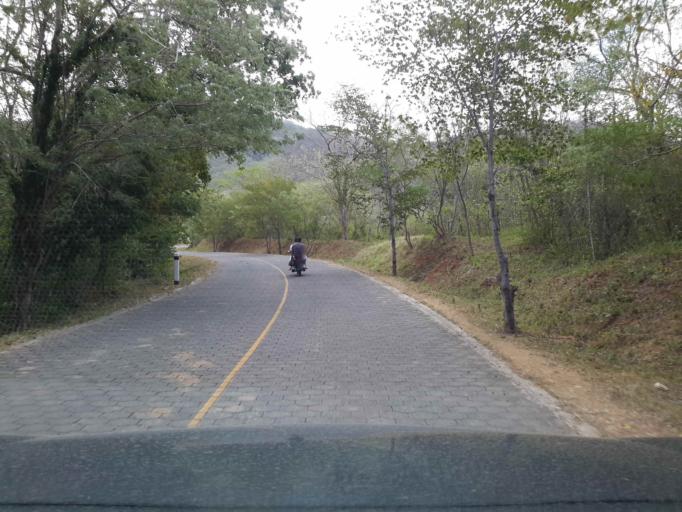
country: NI
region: Rivas
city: San Juan del Sur
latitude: 11.2308
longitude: -85.8261
